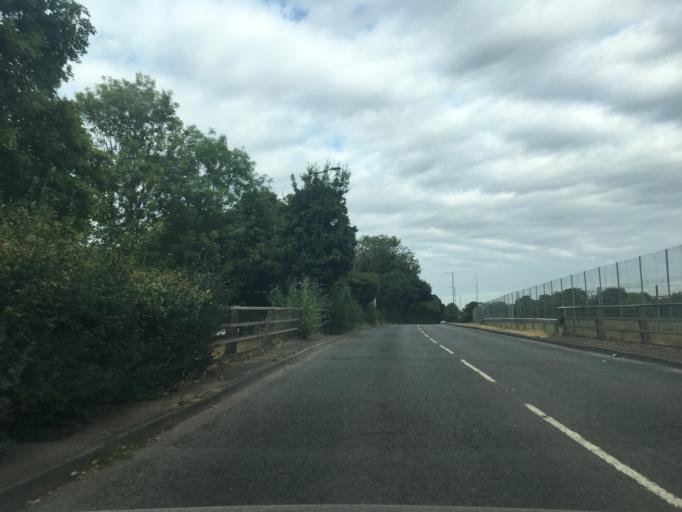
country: GB
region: England
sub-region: Hertfordshire
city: Hemel Hempstead
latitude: 51.7701
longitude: -0.4538
